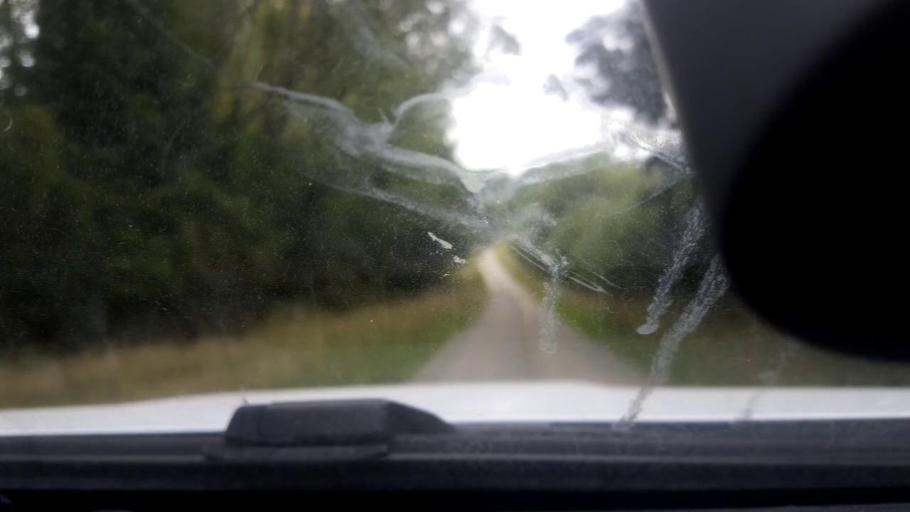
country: NZ
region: Canterbury
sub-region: Timaru District
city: Pleasant Point
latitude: -44.1312
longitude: 171.0842
